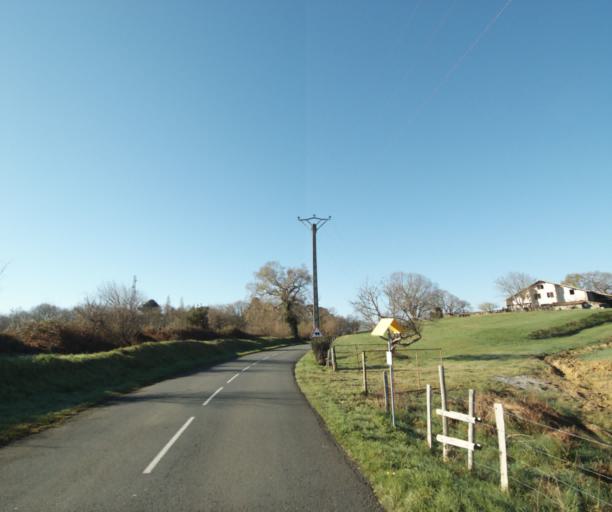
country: FR
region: Aquitaine
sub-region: Departement des Pyrenees-Atlantiques
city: Ciboure
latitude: 43.3575
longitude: -1.6648
